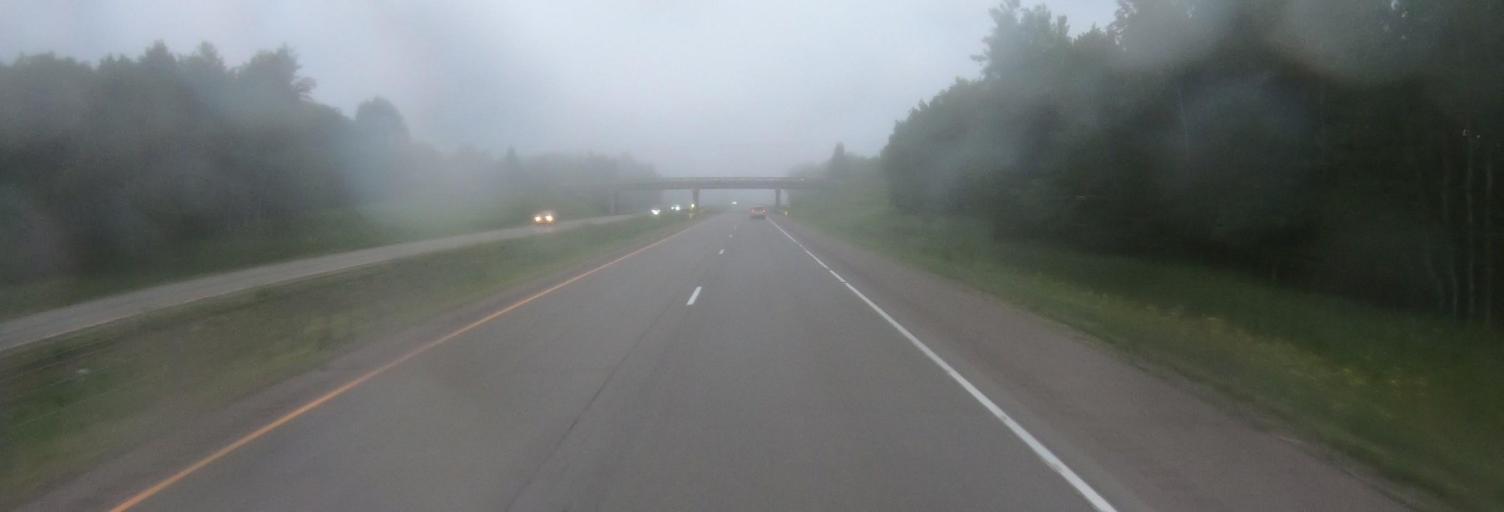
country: US
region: Minnesota
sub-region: Carlton County
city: Carlton
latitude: 46.5758
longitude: -92.5851
